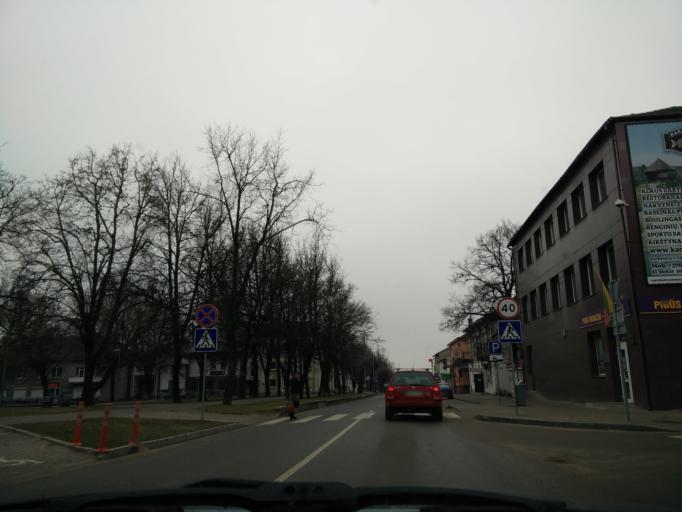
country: LT
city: Raseiniai
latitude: 55.3818
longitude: 23.1168
